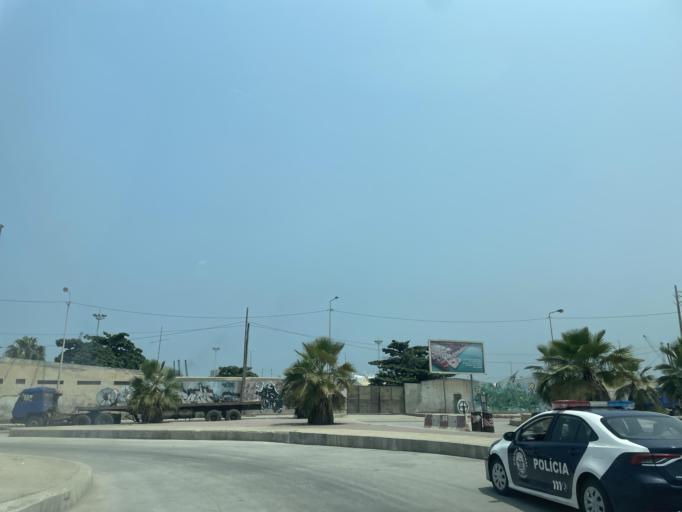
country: AO
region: Luanda
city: Luanda
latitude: -8.8042
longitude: 13.2454
